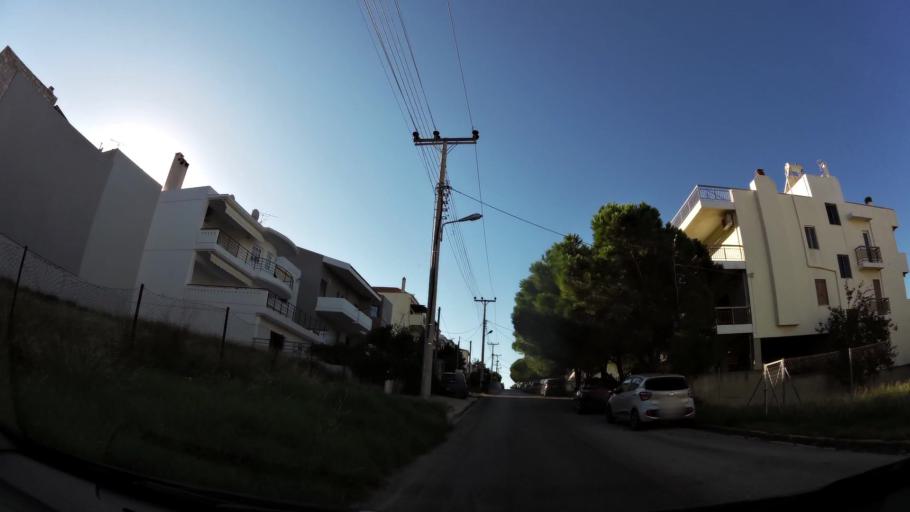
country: GR
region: Attica
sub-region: Nomarchia Athinas
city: Glyfada
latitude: 37.8779
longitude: 23.7714
